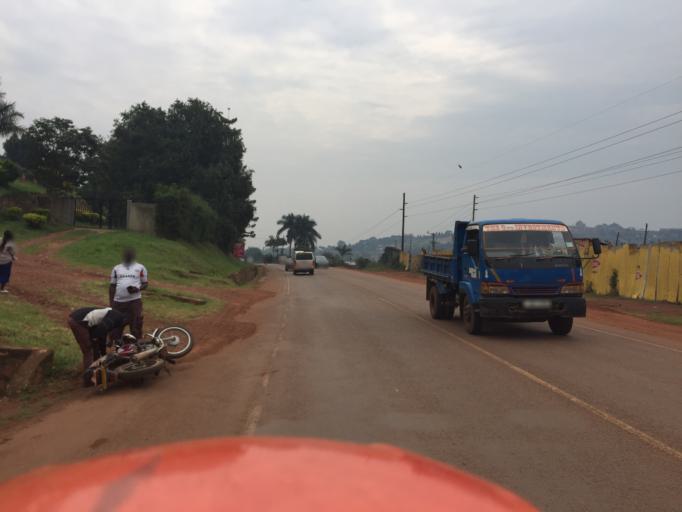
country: UG
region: Central Region
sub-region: Wakiso District
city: Kajansi
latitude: 0.1757
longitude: 32.5387
